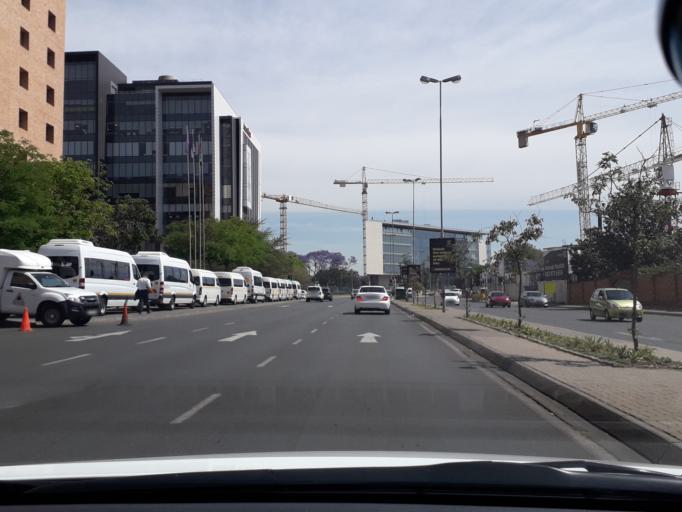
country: ZA
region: Gauteng
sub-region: City of Johannesburg Metropolitan Municipality
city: Johannesburg
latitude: -26.1440
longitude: 28.0438
